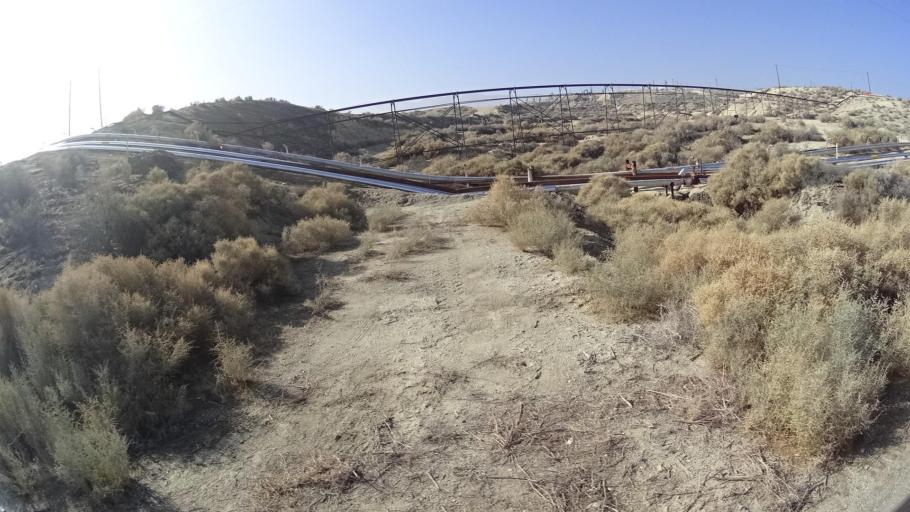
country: US
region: California
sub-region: Kern County
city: Taft Heights
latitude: 35.1530
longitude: -119.5190
